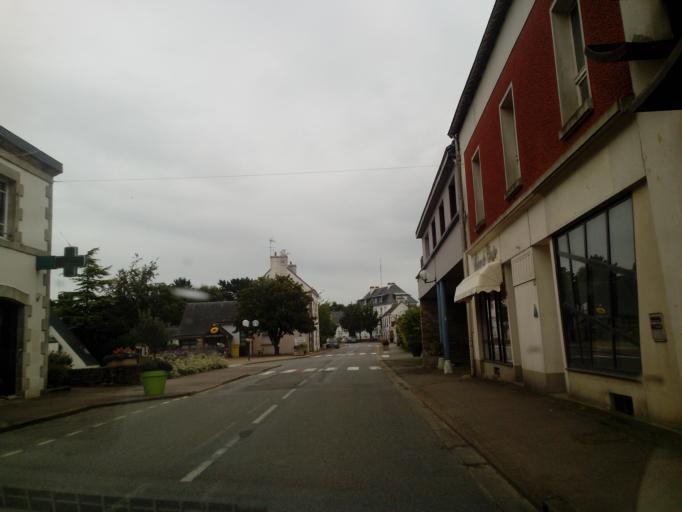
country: FR
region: Brittany
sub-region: Departement du Finistere
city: Arzano
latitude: 47.9010
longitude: -3.4411
